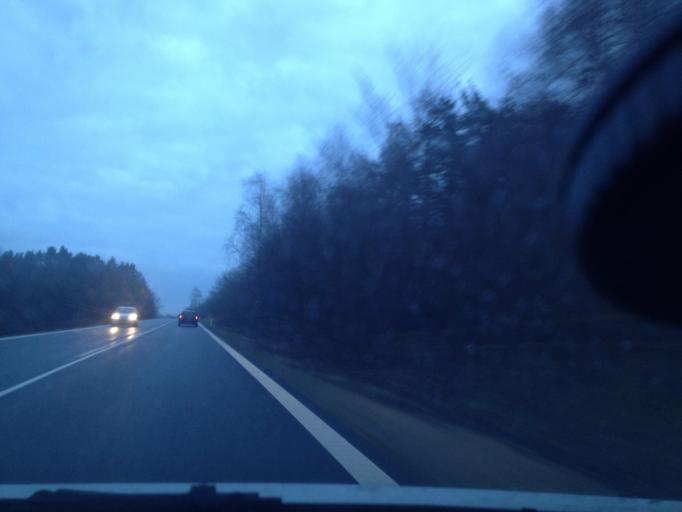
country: DK
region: Capital Region
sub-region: Rudersdal Kommune
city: Birkerod
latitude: 55.8958
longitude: 12.4287
